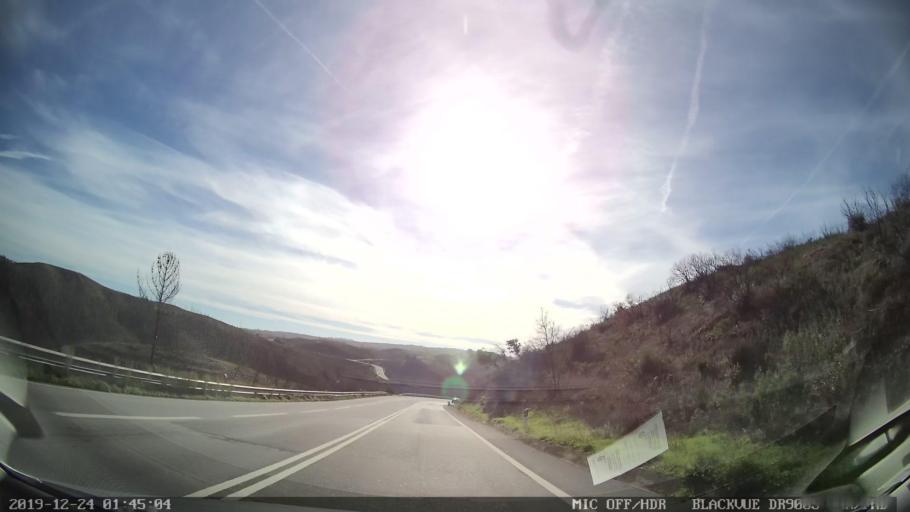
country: PT
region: Portalegre
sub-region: Nisa
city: Nisa
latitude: 39.5483
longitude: -7.7977
